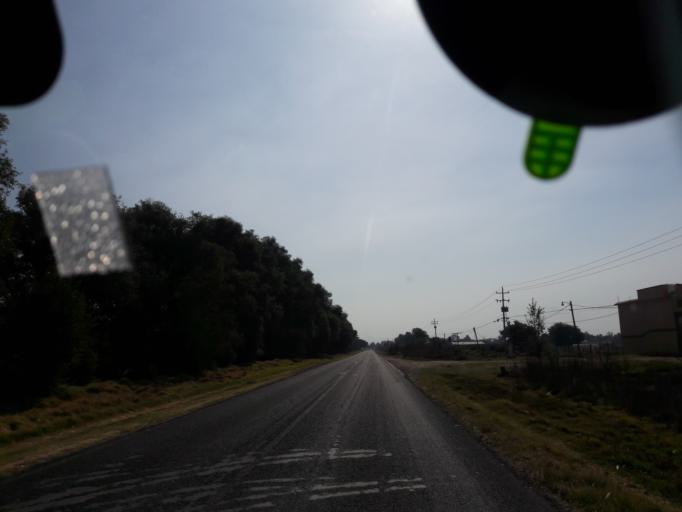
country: MX
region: Tlaxcala
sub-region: Ixtacuixtla de Mariano Matamoros
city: Santa Justina Ecatepec
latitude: 19.3082
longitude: -98.3640
